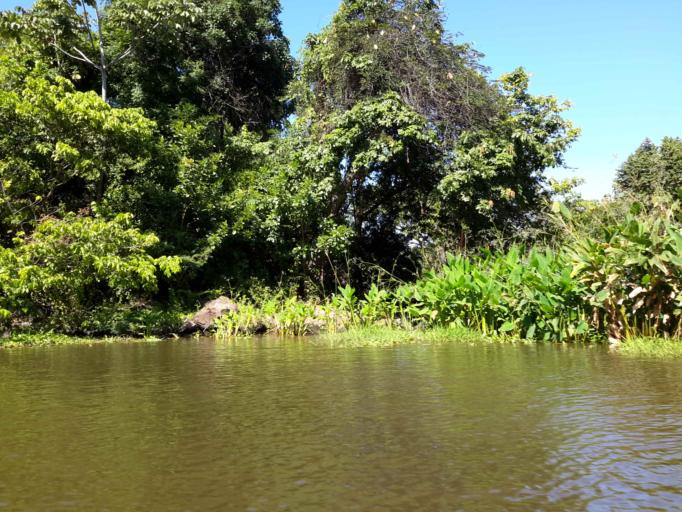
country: NI
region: Granada
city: Granada
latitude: 11.9111
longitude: -85.9279
